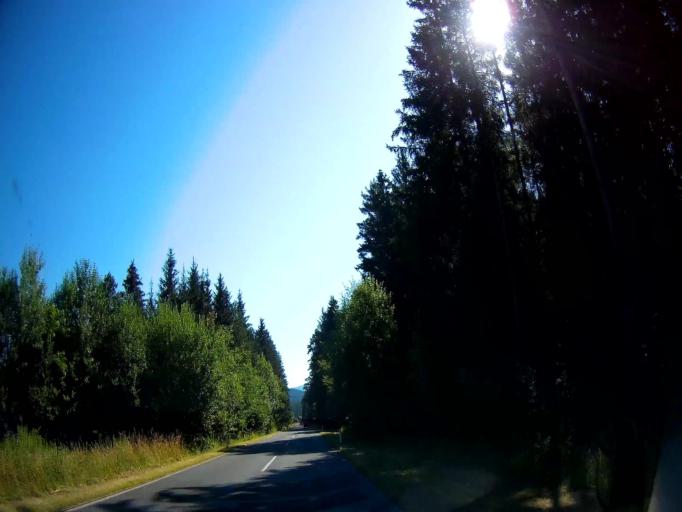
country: AT
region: Carinthia
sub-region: Politischer Bezirk Volkermarkt
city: Feistritz ob Bleiburg
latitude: 46.5760
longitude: 14.7549
